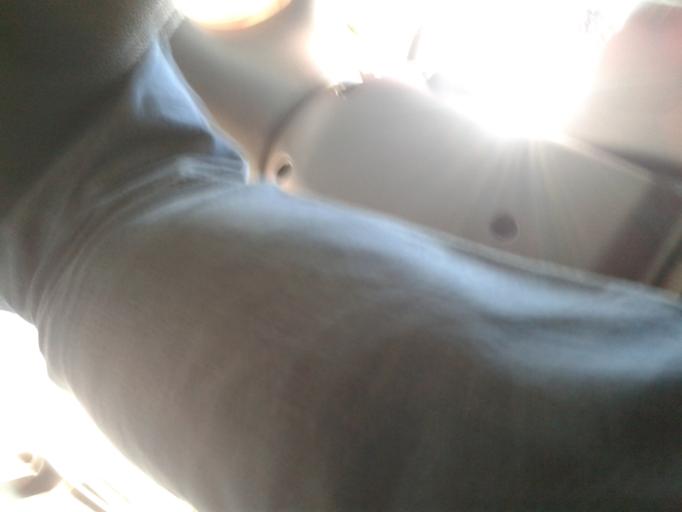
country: BR
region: Minas Gerais
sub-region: Ituiutaba
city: Ituiutaba
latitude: -19.0816
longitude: -49.7450
